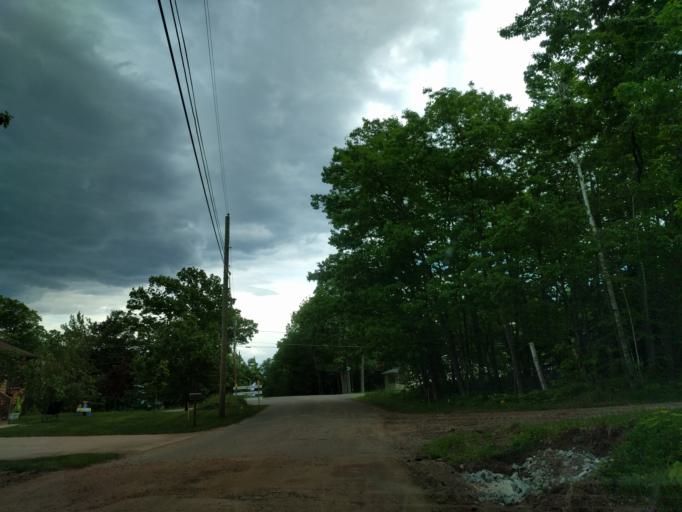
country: US
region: Michigan
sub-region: Marquette County
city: Trowbridge Park
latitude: 46.5572
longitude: -87.4435
